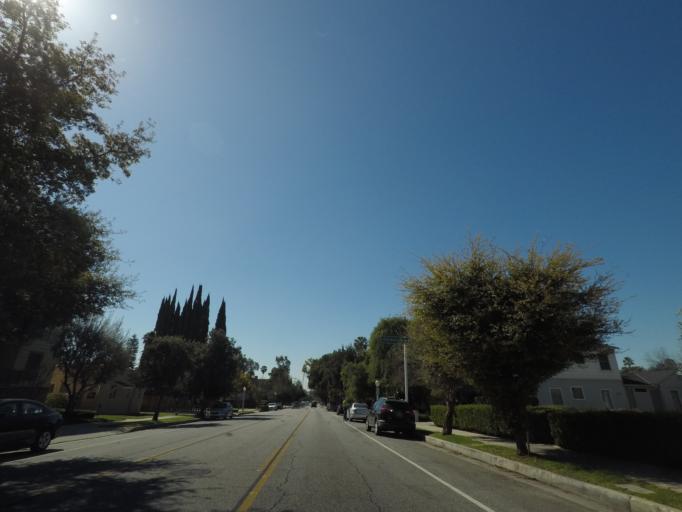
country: US
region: California
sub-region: Los Angeles County
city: Pasadena
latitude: 34.1372
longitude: -118.1413
